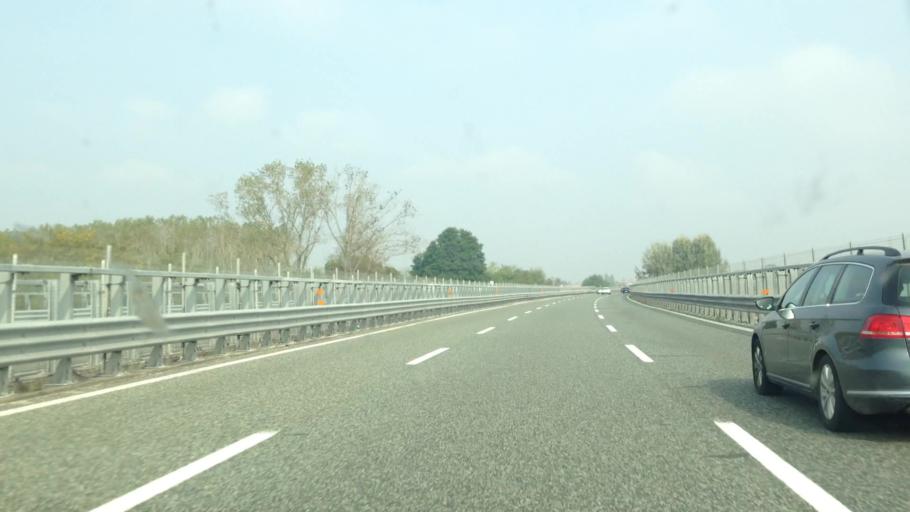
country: IT
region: Piedmont
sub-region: Provincia di Alessandria
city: Villanova Monferrato
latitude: 45.1505
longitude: 8.4839
